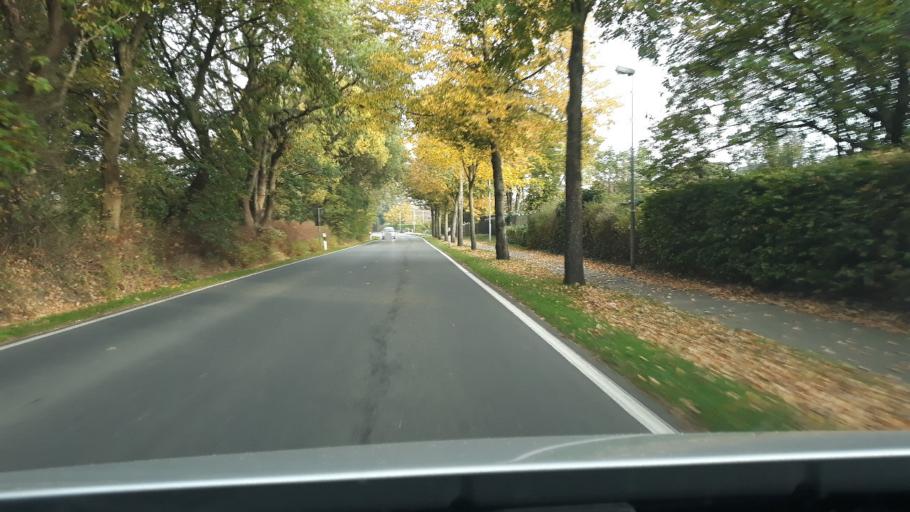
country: DE
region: Schleswig-Holstein
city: Kropp
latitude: 54.4048
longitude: 9.5111
